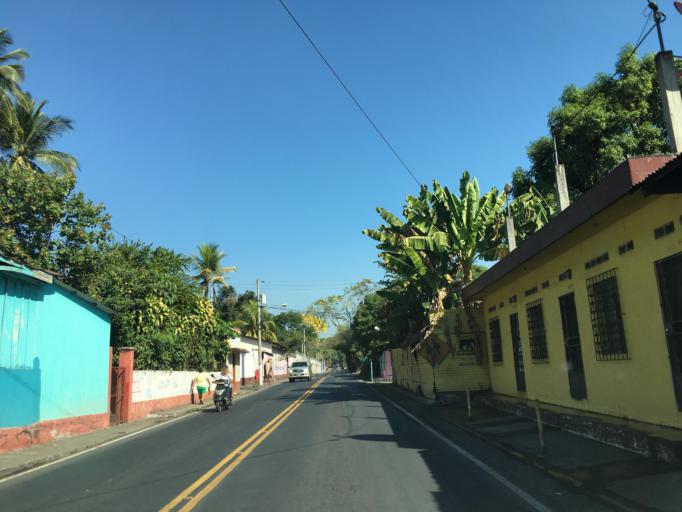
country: GT
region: Escuintla
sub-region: Municipio de La Democracia
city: La Democracia
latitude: 14.2298
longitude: -90.9493
